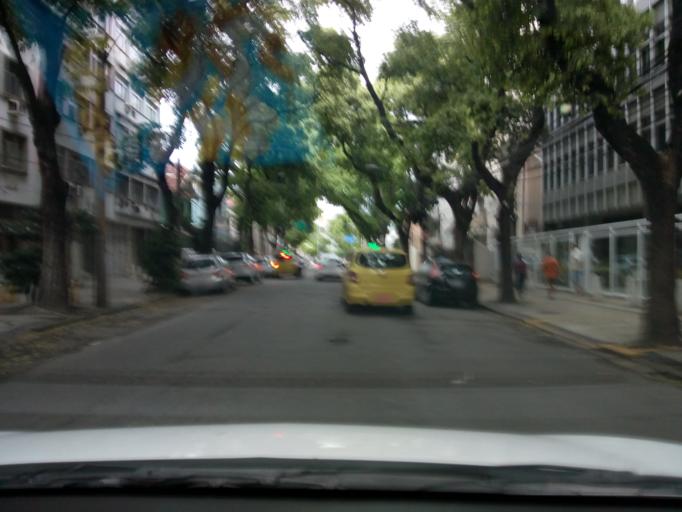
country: BR
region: Rio de Janeiro
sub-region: Rio De Janeiro
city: Rio de Janeiro
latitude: -22.9194
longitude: -43.2260
